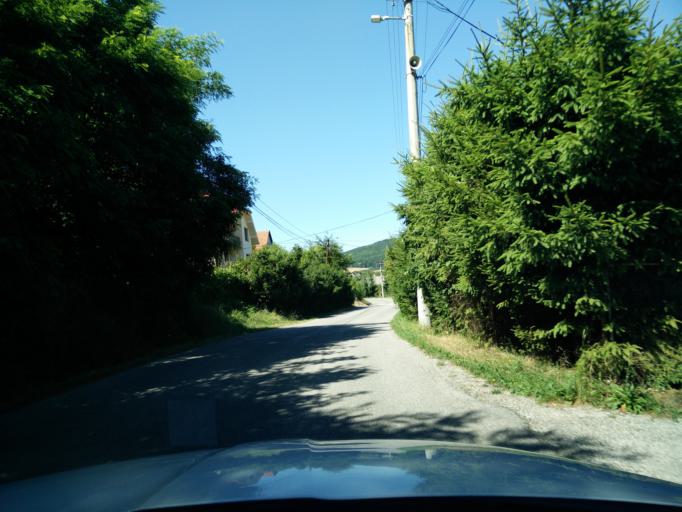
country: SK
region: Nitriansky
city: Prievidza
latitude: 48.7914
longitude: 18.6990
